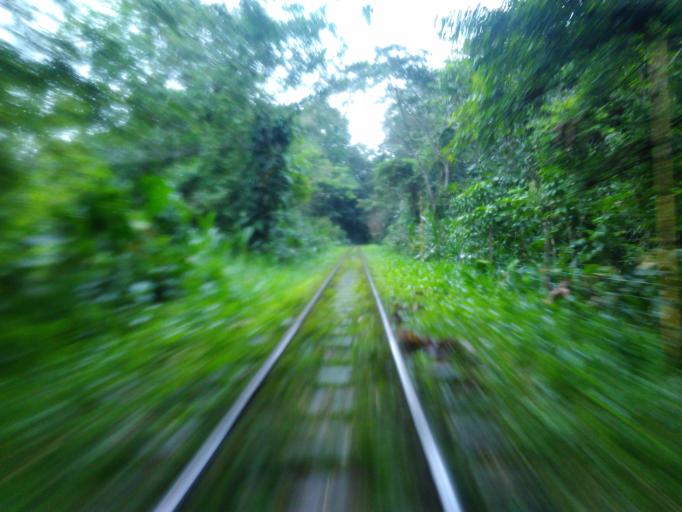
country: CO
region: Valle del Cauca
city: Buenaventura
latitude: 3.8537
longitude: -76.8559
